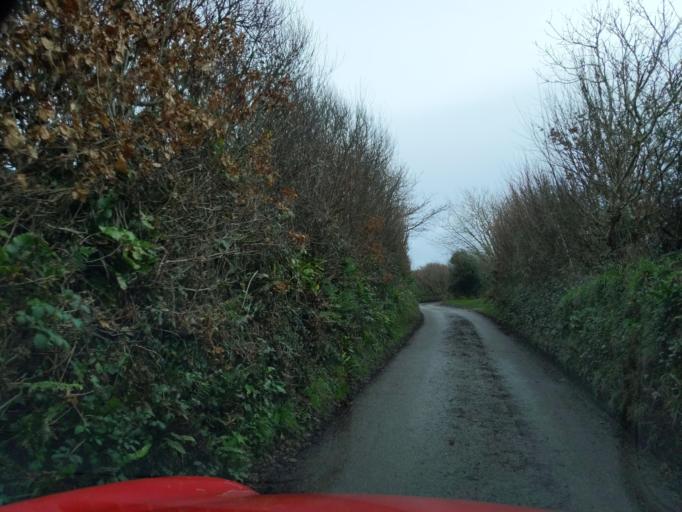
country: GB
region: England
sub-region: Cornwall
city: Duloe
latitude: 50.3546
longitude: -4.5157
